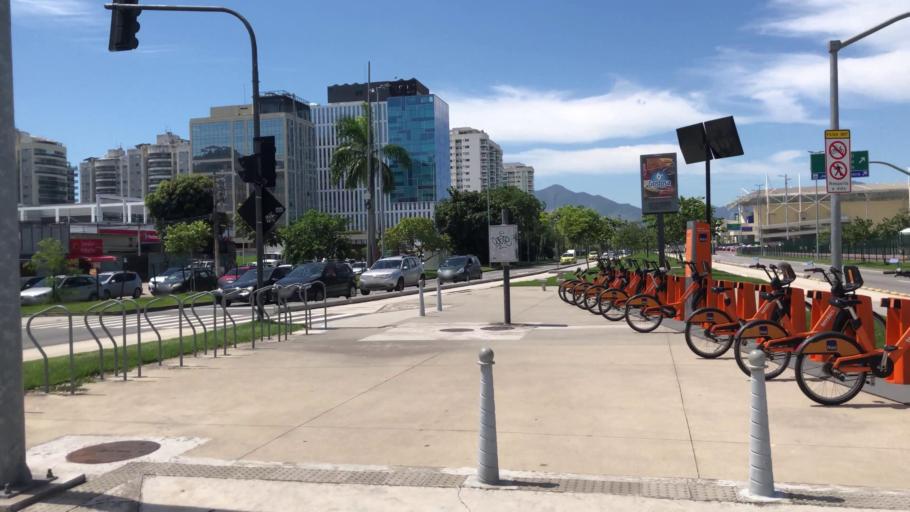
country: BR
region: Rio de Janeiro
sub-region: Nilopolis
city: Nilopolis
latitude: -22.9951
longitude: -43.4223
